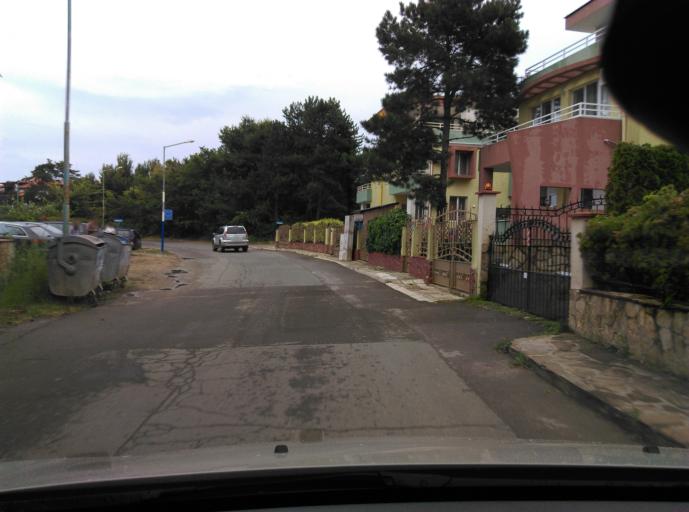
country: BG
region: Burgas
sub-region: Obshtina Sozopol
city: Sozopol
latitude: 42.4062
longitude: 27.7149
